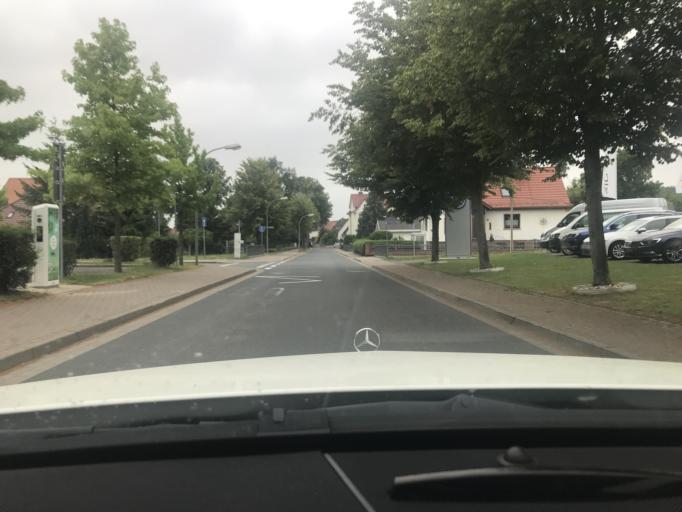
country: DE
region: Thuringia
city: Worbis
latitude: 51.4199
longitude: 10.3683
